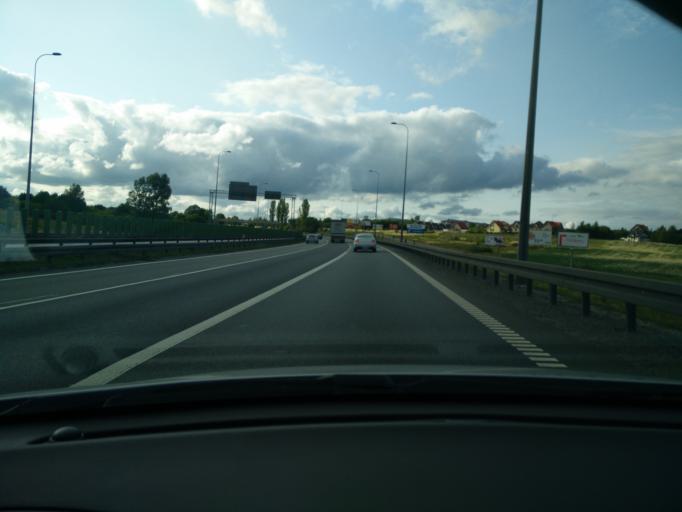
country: PL
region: Pomeranian Voivodeship
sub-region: Powiat gdanski
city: Straszyn
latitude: 54.2944
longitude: 18.5847
